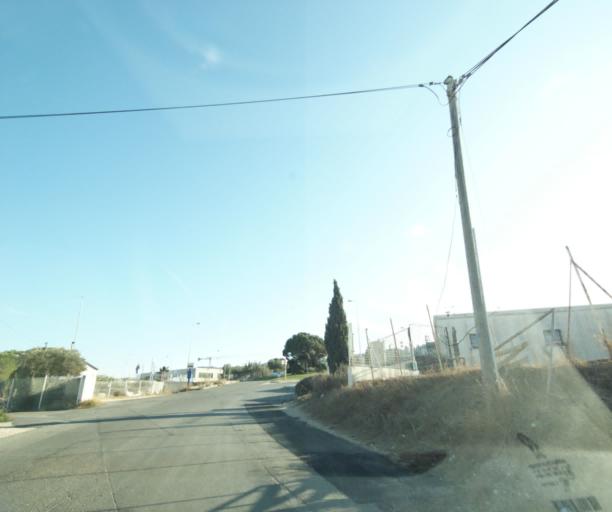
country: FR
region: Provence-Alpes-Cote d'Azur
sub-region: Departement des Bouches-du-Rhone
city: Chateauneuf-les-Martigues
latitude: 43.3950
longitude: 5.1365
